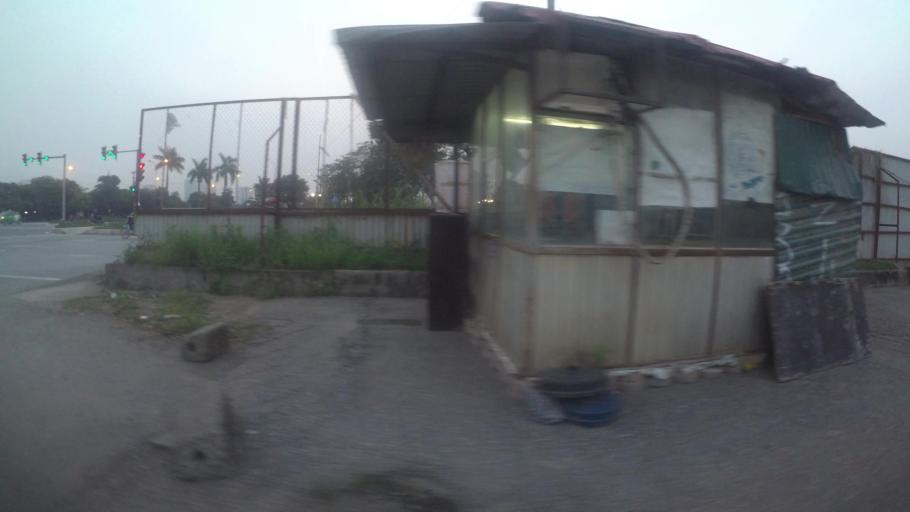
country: VN
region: Ha Noi
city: Tay Ho
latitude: 21.0630
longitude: 105.7900
